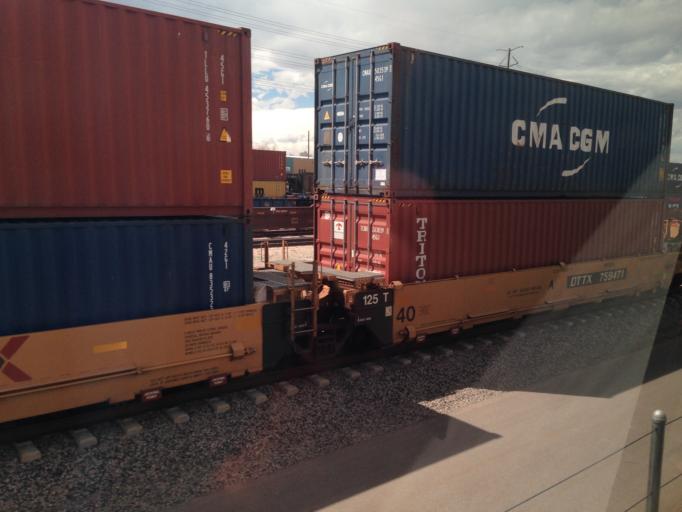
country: US
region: Colorado
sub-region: Denver County
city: Denver
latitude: 39.7734
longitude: -104.9972
